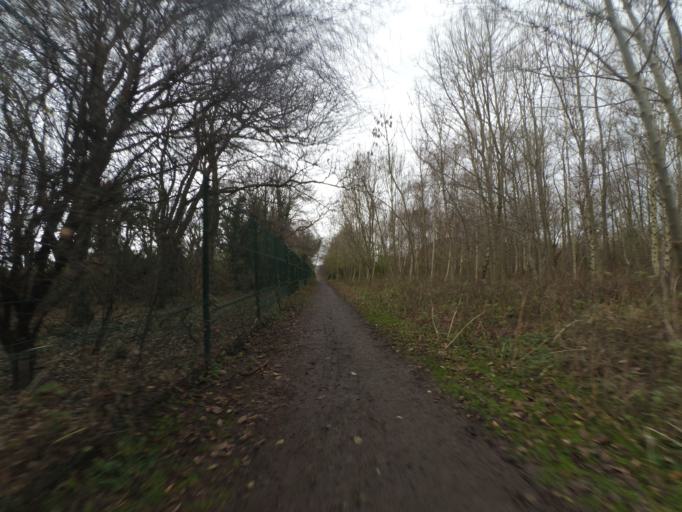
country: GB
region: Scotland
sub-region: West Lothian
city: Seafield
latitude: 55.9268
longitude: -3.1480
